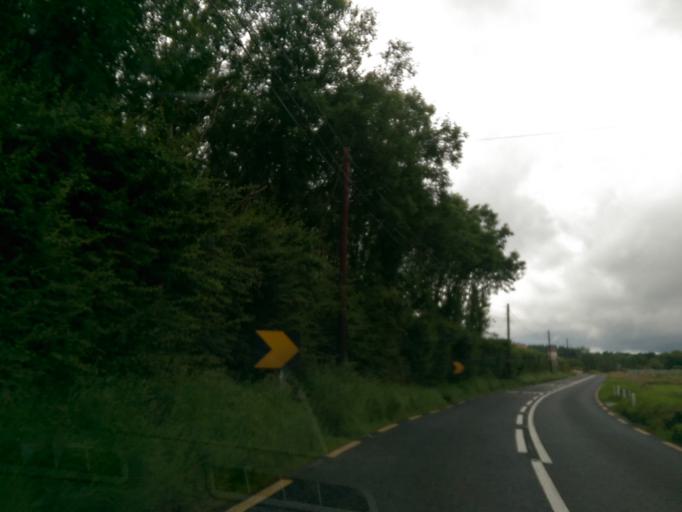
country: IE
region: Munster
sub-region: An Clar
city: Ennis
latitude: 52.7680
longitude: -9.0984
